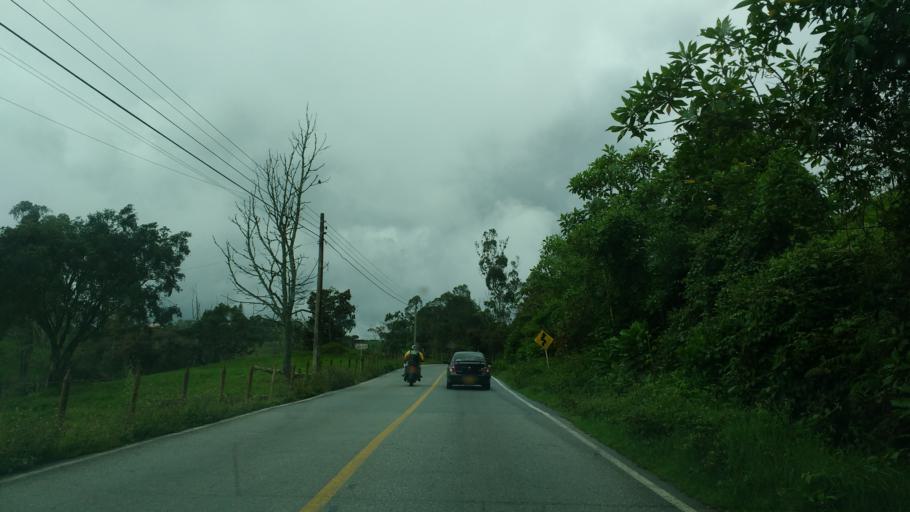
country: CO
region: Antioquia
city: Marinilla
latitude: 6.1973
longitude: -75.2856
